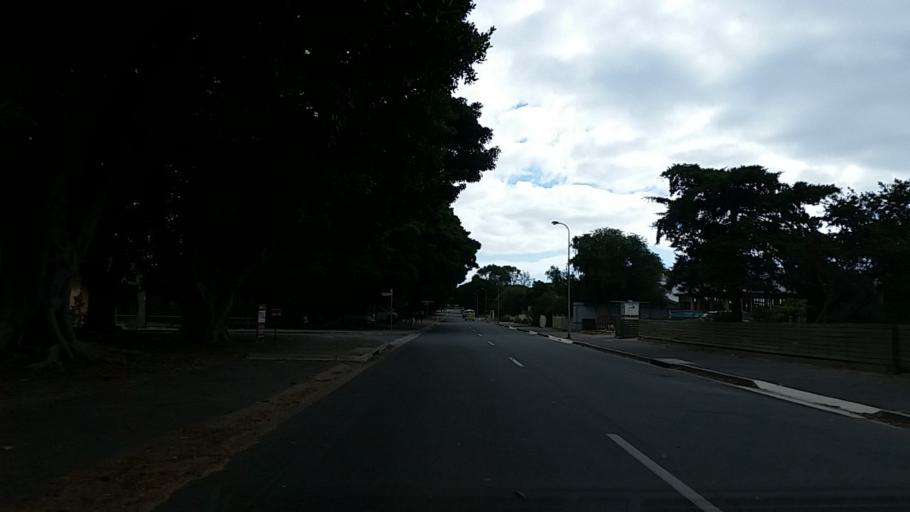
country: AU
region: South Australia
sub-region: Yankalilla
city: Normanville
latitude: -35.4451
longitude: 138.3144
